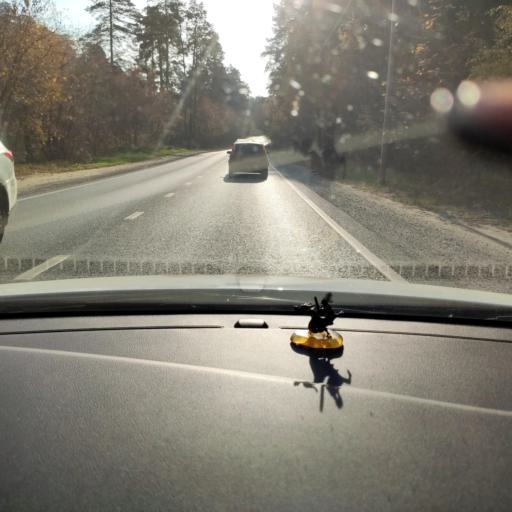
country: RU
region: Tatarstan
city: Osinovo
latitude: 55.8288
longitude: 48.8936
